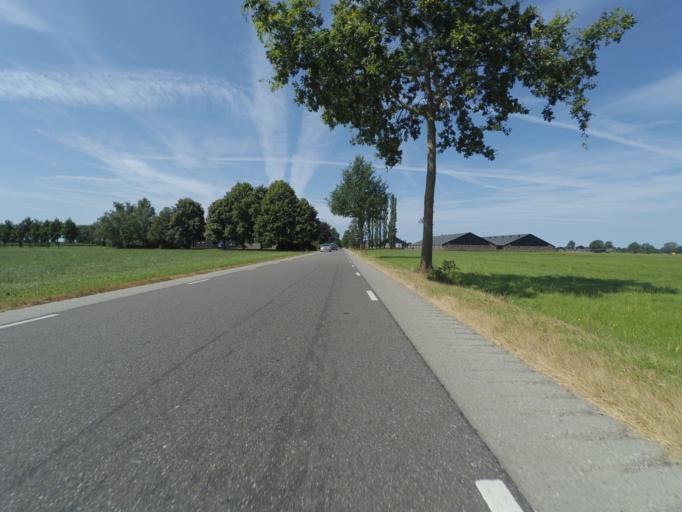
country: NL
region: Gelderland
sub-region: Gemeente Barneveld
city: Kootwijkerbroek
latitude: 52.1434
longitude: 5.6932
